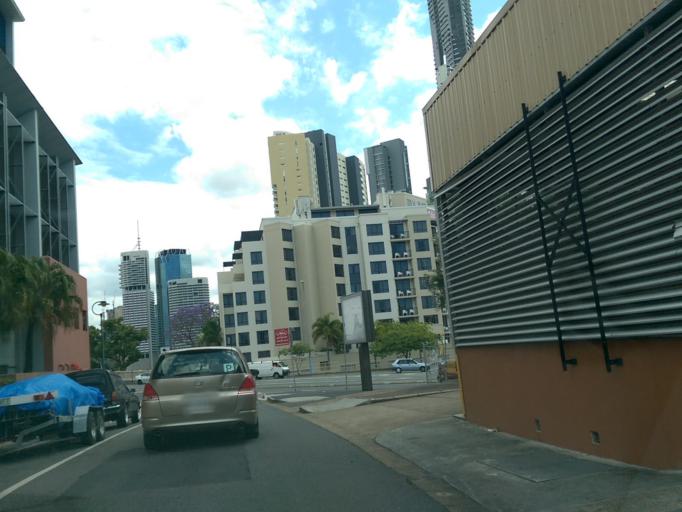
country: AU
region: Queensland
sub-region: Brisbane
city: Fortitude Valley
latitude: -27.4609
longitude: 153.0361
